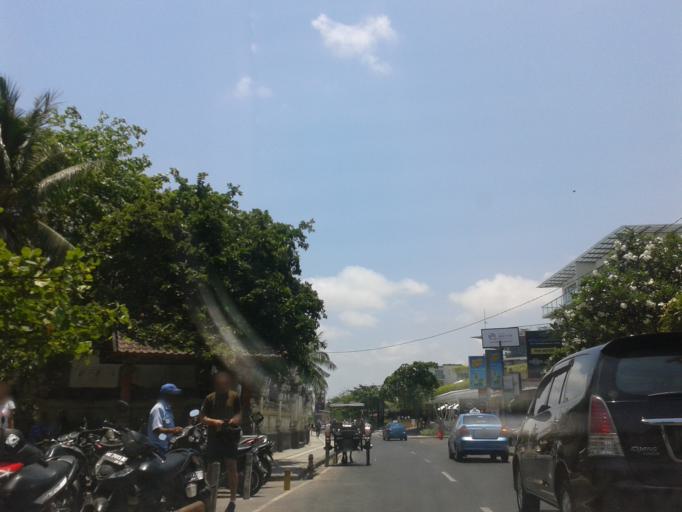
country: ID
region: Bali
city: Kuta
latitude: -8.7190
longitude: 115.1692
